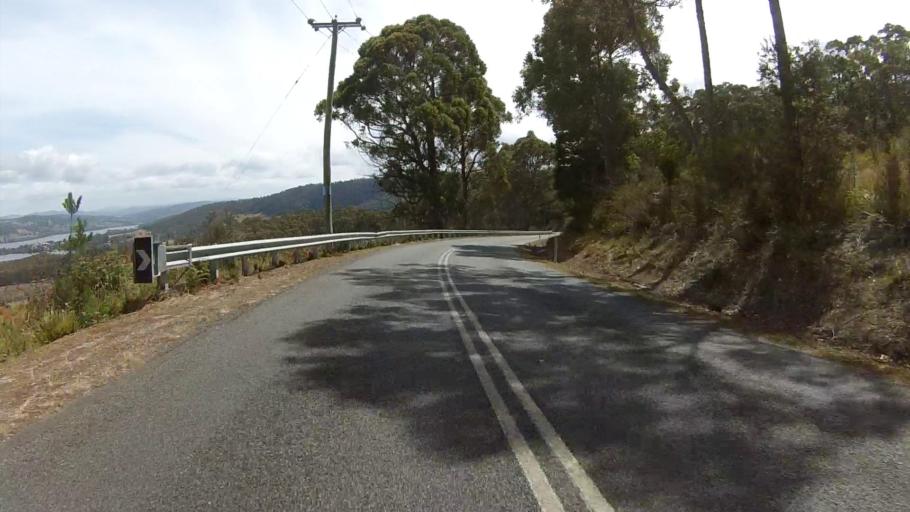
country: AU
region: Tasmania
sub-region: Huon Valley
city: Cygnet
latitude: -43.2254
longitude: 147.1278
